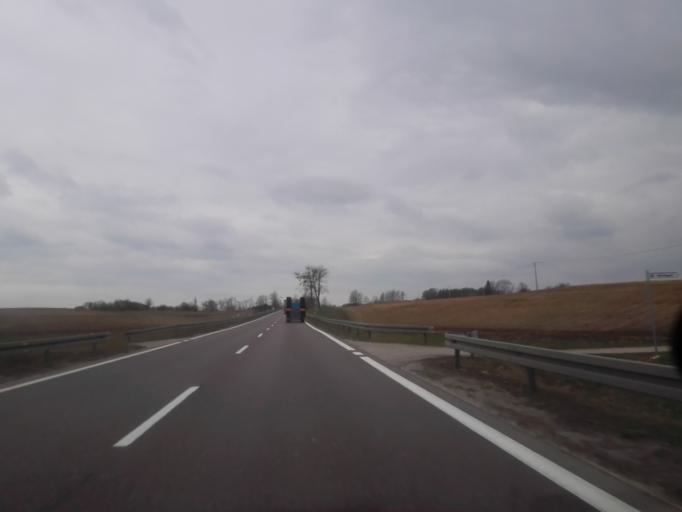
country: PL
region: Podlasie
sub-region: Powiat augustowski
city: Augustow
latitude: 53.8018
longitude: 22.8897
